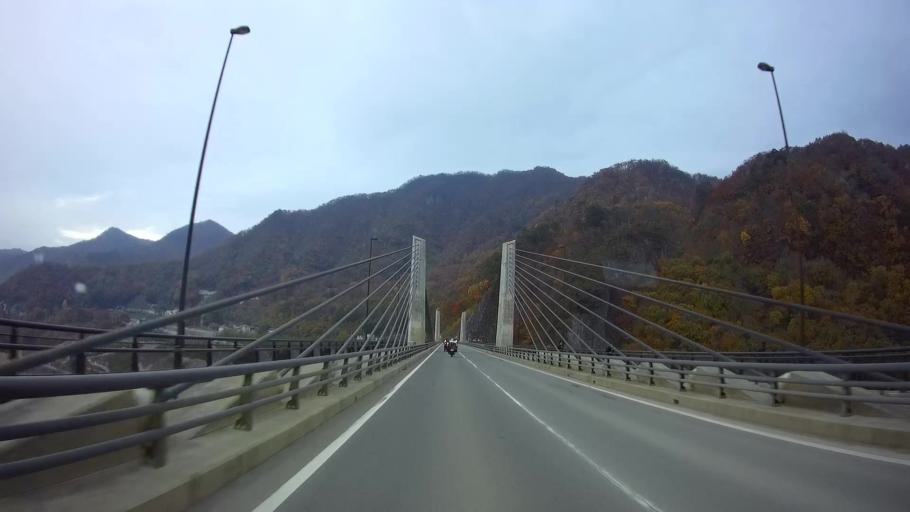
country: JP
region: Gunma
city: Nakanojomachi
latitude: 36.5455
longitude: 138.6874
